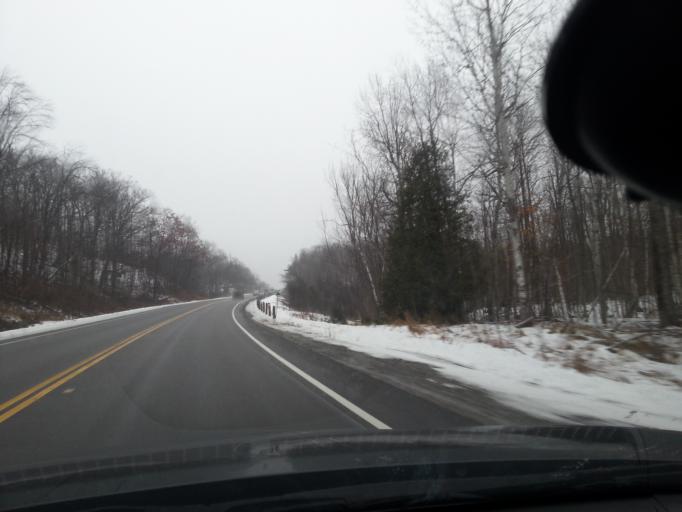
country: CA
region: Ontario
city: Perth
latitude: 44.7838
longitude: -76.7206
